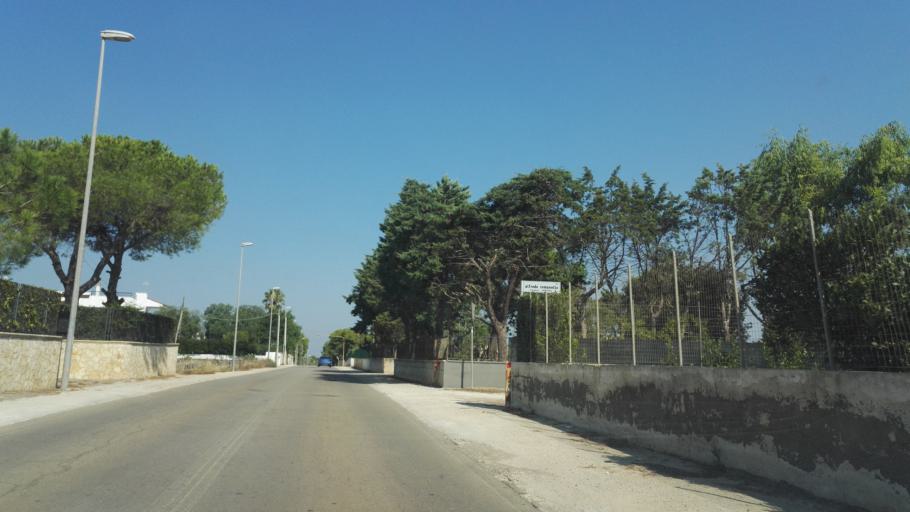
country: IT
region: Apulia
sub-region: Provincia di Lecce
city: Nardo
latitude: 40.1435
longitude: 18.0091
